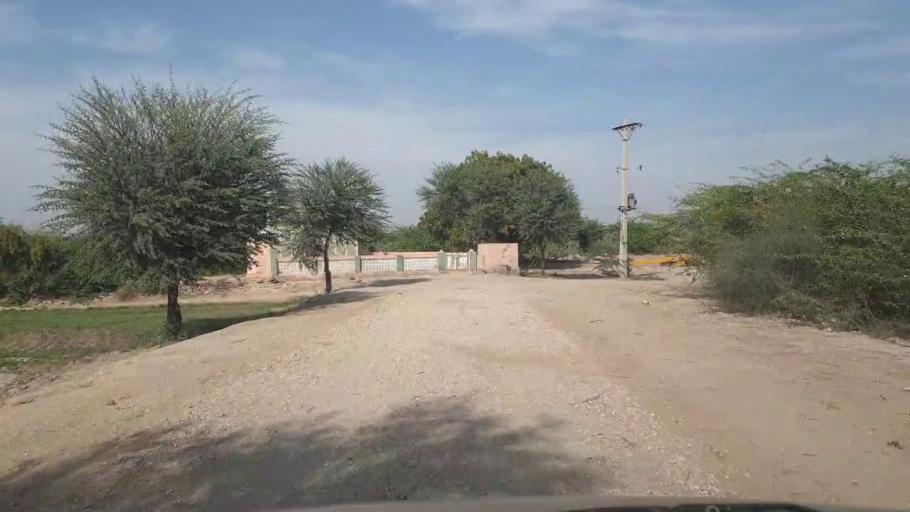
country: PK
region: Sindh
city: Nabisar
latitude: 25.1641
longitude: 69.6681
